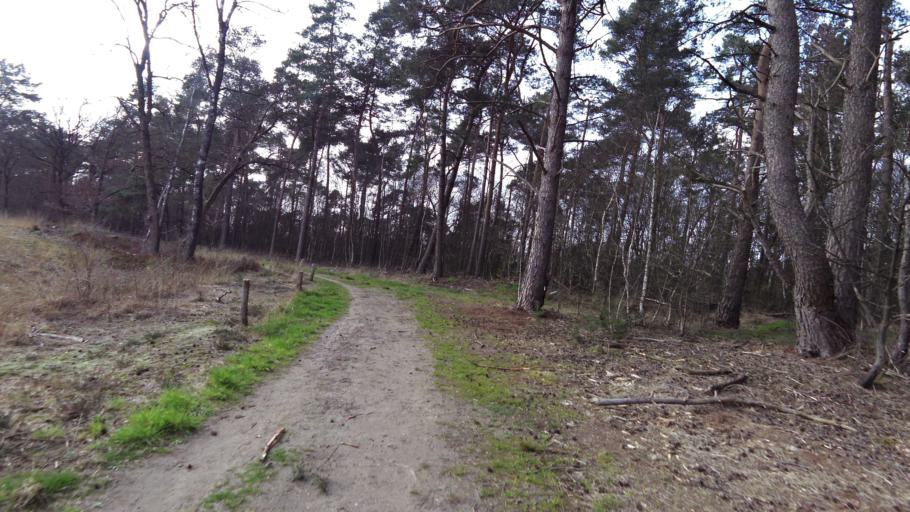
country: NL
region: Gelderland
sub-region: Gemeente Barneveld
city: Voorthuizen
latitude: 52.1936
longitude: 5.5710
